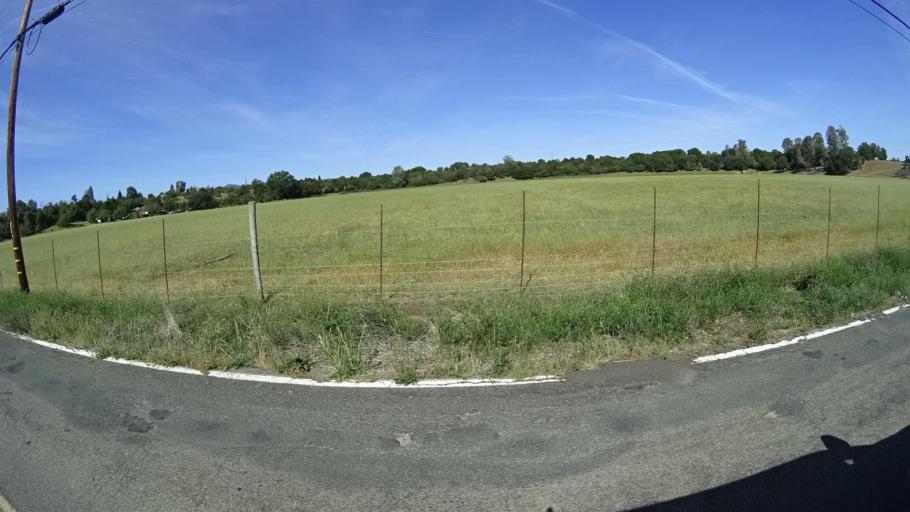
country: US
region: California
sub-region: Lake County
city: Kelseyville
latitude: 38.9667
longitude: -122.8382
